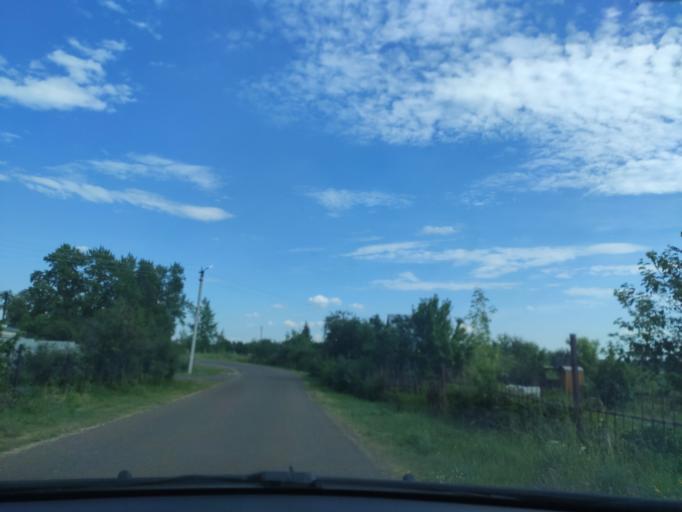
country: RU
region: Ulyanovsk
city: Cherdakly
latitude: 54.4407
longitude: 48.9037
